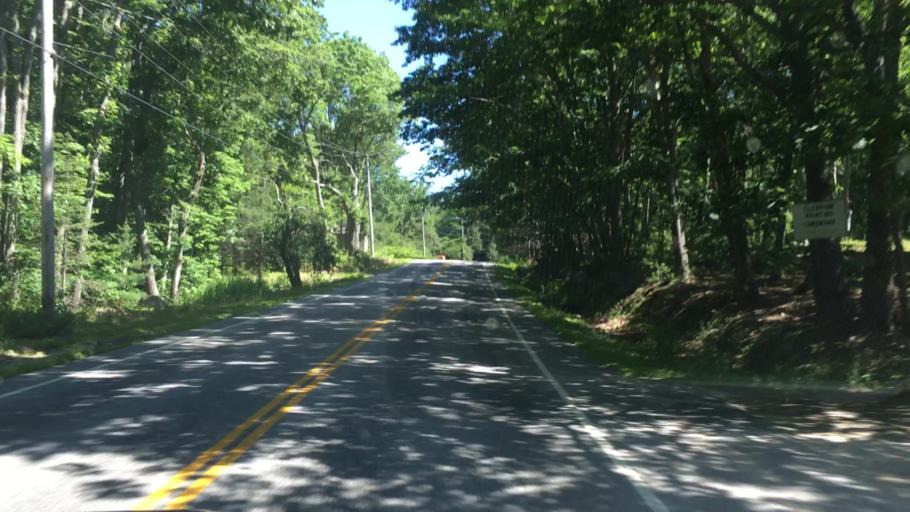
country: US
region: Maine
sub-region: Hancock County
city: Sedgwick
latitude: 44.3477
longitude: -68.6728
